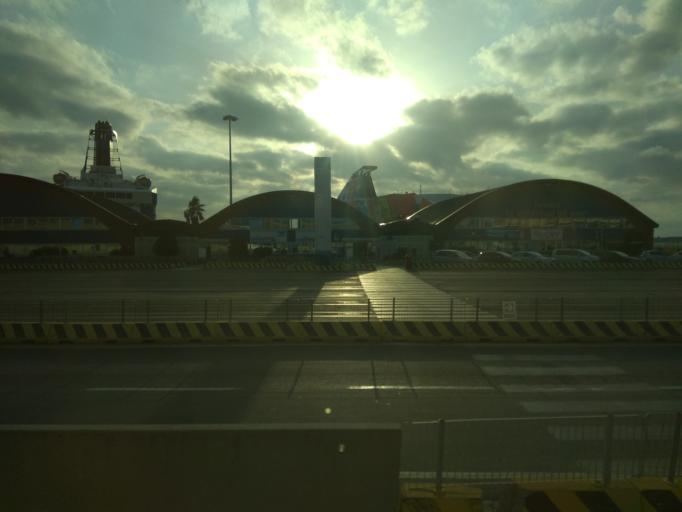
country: IT
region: Latium
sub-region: Citta metropolitana di Roma Capitale
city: Civitavecchia
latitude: 42.0993
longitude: 11.7844
